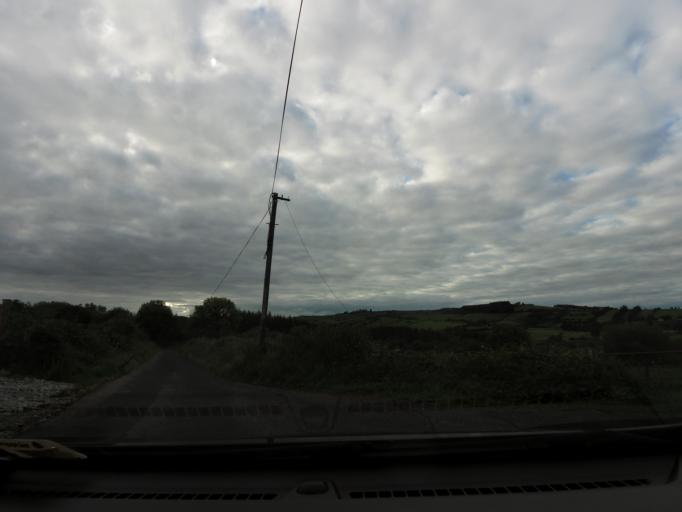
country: IE
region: Connaught
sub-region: County Galway
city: Loughrea
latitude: 53.1405
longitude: -8.5296
